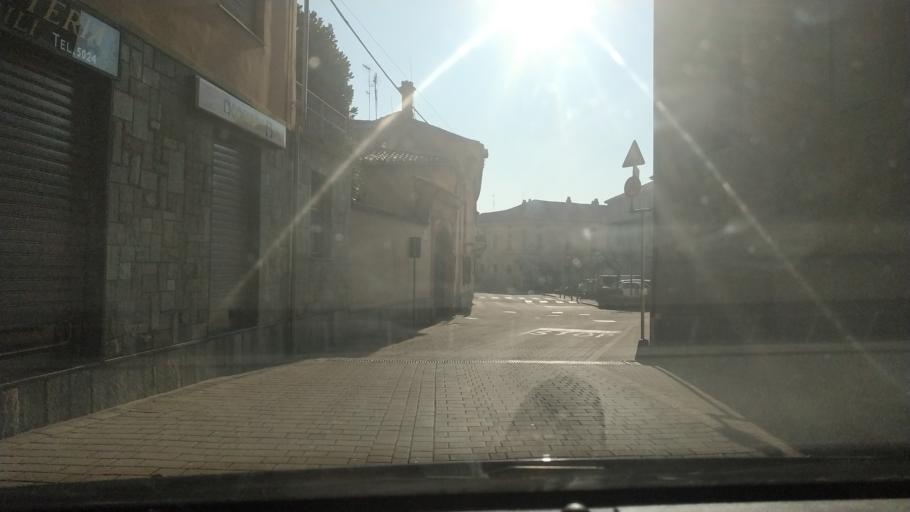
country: IT
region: Piedmont
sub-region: Provincia di Torino
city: Pavone Canavese
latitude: 45.4358
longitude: 7.8544
